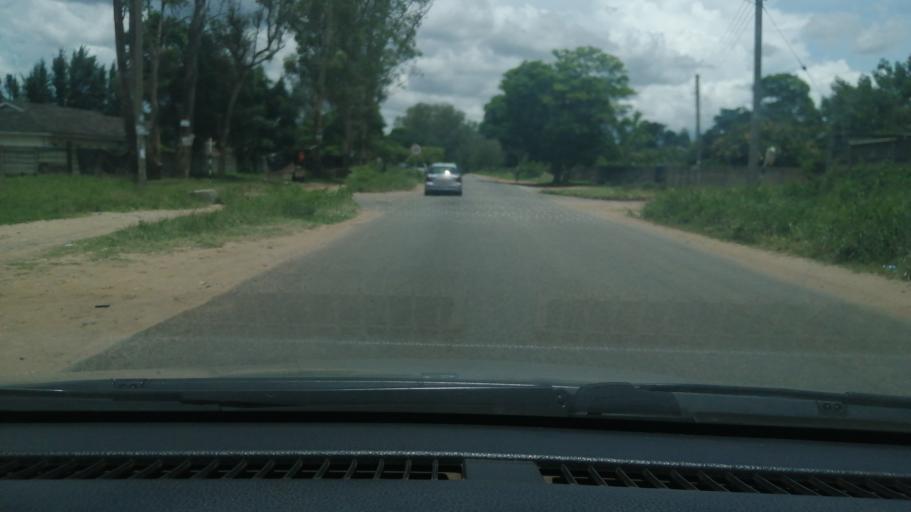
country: ZW
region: Harare
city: Harare
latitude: -17.8836
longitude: 31.0759
